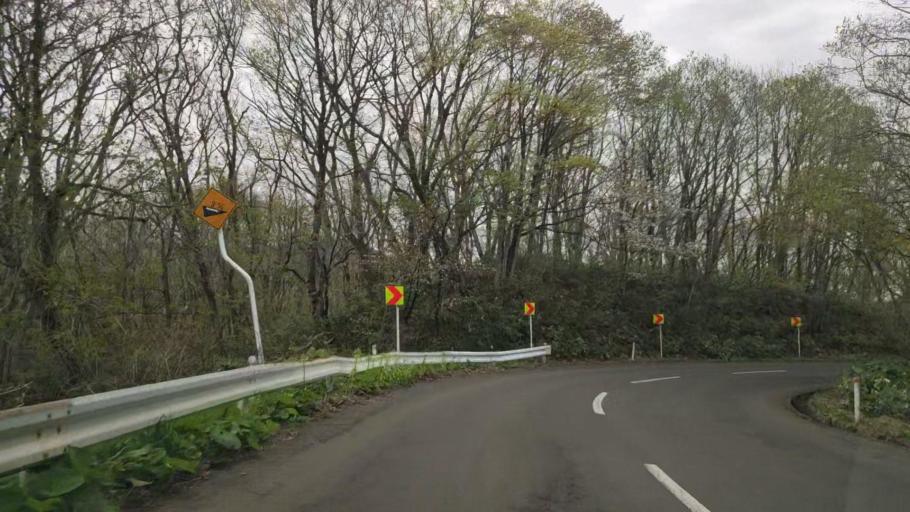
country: JP
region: Akita
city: Hanawa
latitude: 40.3752
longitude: 140.7901
